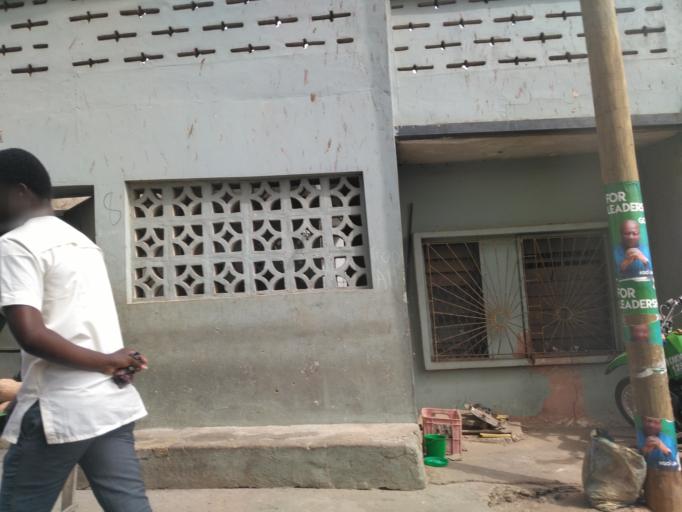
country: GH
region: Ashanti
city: Kumasi
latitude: 6.6997
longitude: -1.6044
